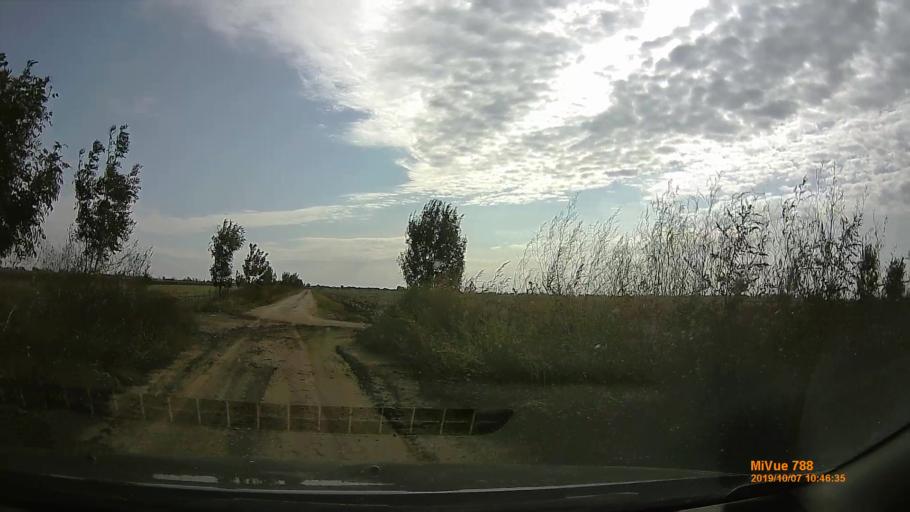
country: HU
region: Bekes
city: Kondoros
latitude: 46.7394
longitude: 20.8182
